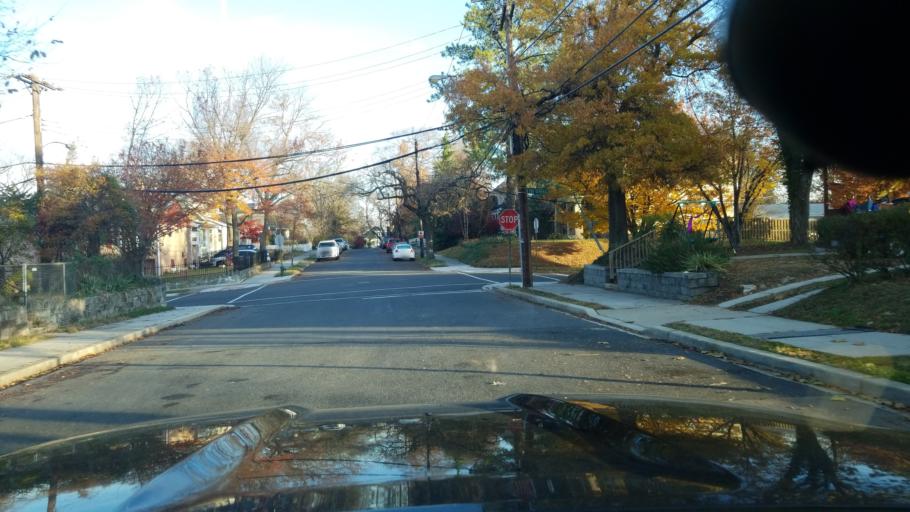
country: US
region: Maryland
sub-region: Montgomery County
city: Takoma Park
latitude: 38.9697
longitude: -77.0117
